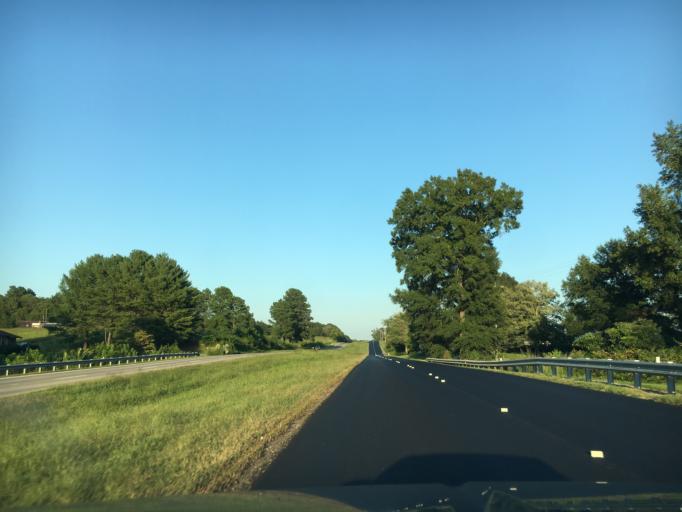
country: US
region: Virginia
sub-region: City of Danville
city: Danville
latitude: 36.5809
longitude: -79.2143
